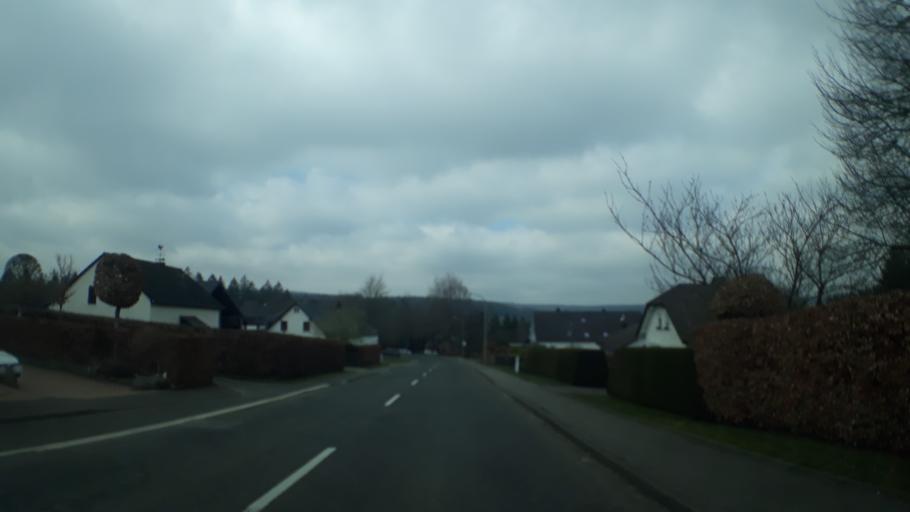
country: DE
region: North Rhine-Westphalia
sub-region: Regierungsbezirk Koln
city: Monschau
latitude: 50.5343
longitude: 6.2065
